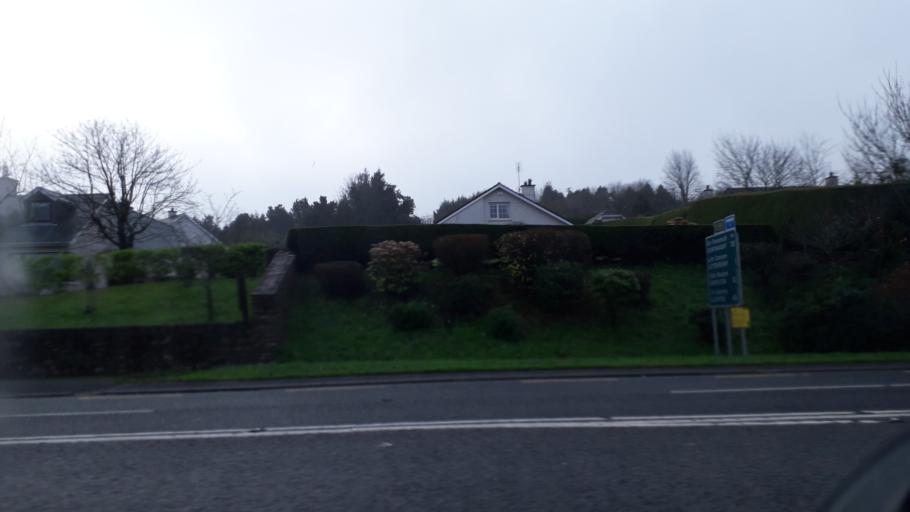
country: IE
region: Ulster
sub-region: County Donegal
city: Letterkenny
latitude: 54.9454
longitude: -7.7026
